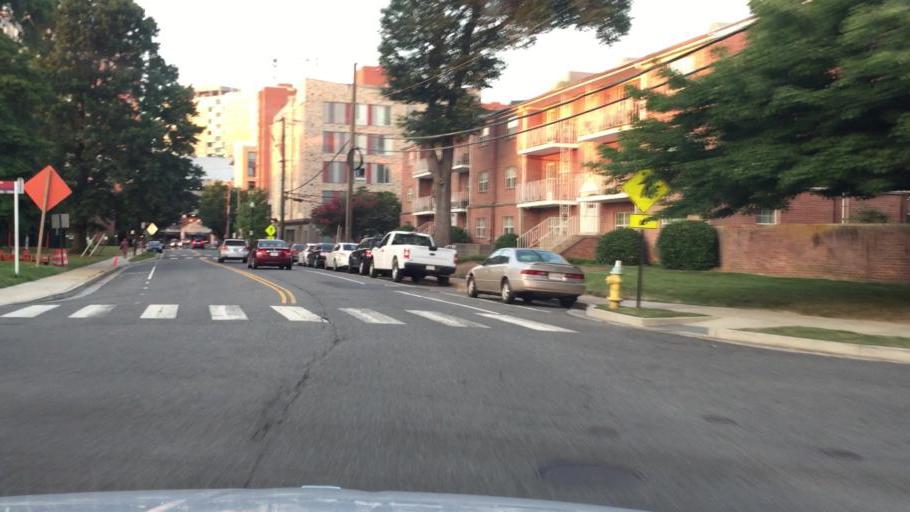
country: US
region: Virginia
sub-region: Arlington County
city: Arlington
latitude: 38.8765
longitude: -77.1140
